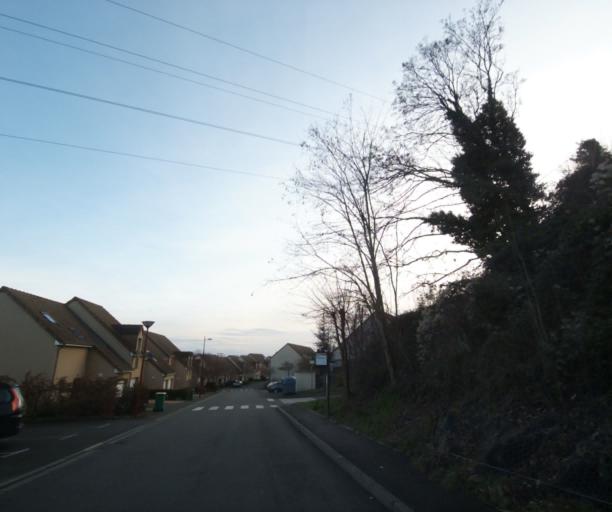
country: FR
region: Pays de la Loire
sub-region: Departement de la Sarthe
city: Le Mans
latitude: 47.9987
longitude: 0.1698
